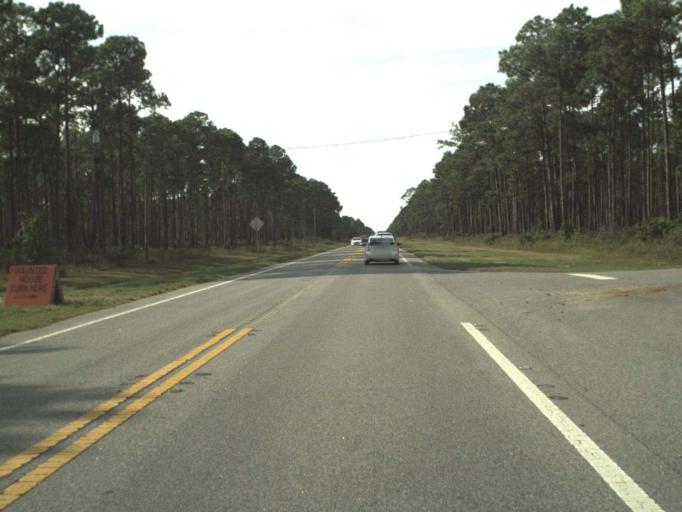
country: US
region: Florida
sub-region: Bay County
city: Mexico Beach
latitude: 29.9987
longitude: -85.4978
